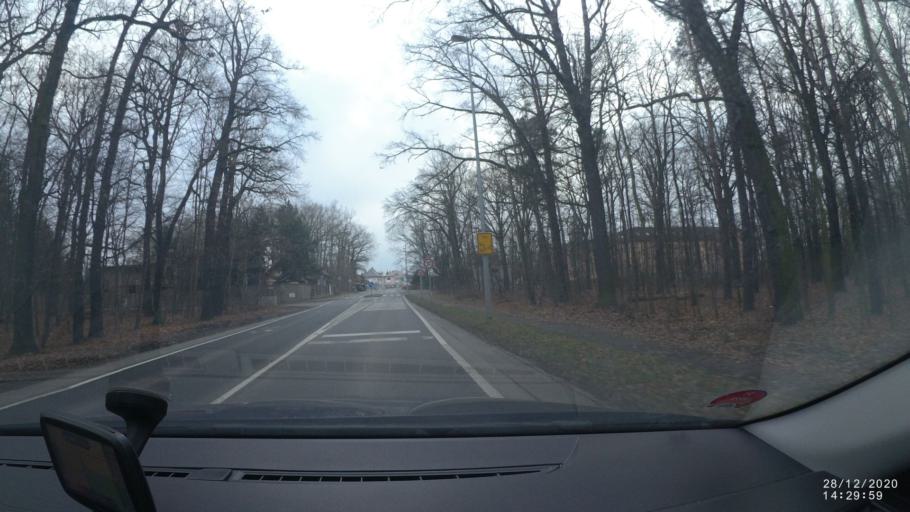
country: CZ
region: Central Bohemia
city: Sestajovice
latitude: 50.0789
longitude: 14.6604
